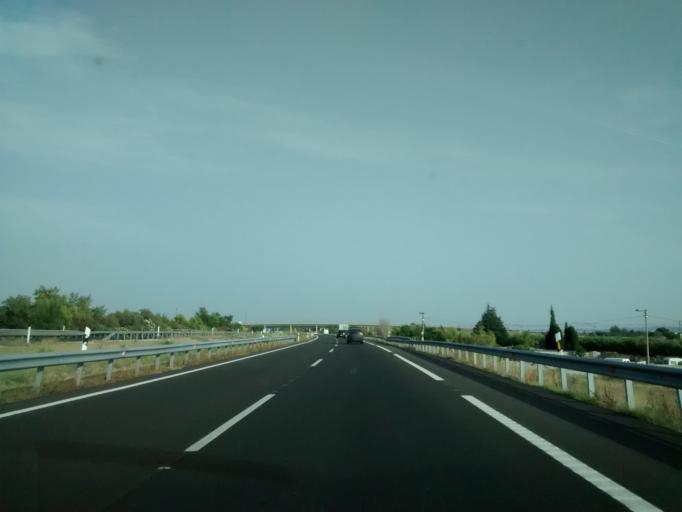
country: ES
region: Aragon
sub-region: Provincia de Zaragoza
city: Utebo
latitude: 41.6978
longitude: -0.9750
